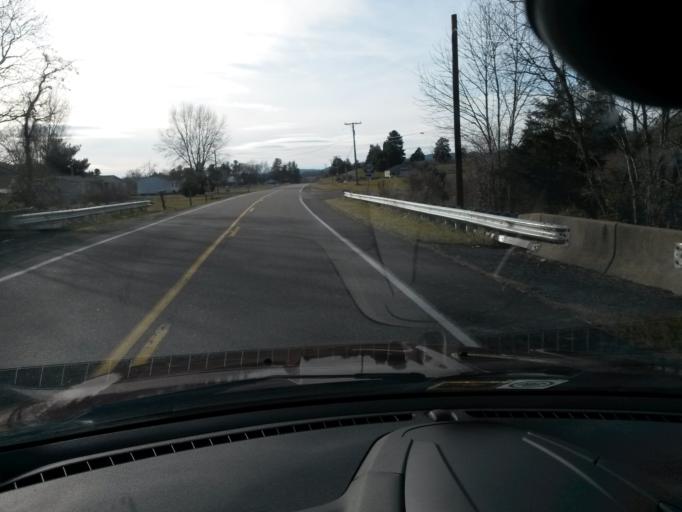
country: US
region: Virginia
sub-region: Augusta County
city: Jolivue
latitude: 38.0982
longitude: -79.3280
